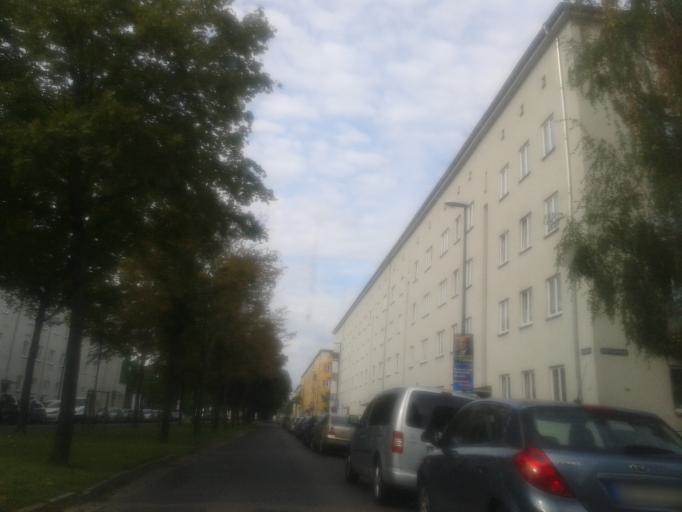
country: DE
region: Saxony
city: Albertstadt
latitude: 51.0368
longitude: 13.7885
